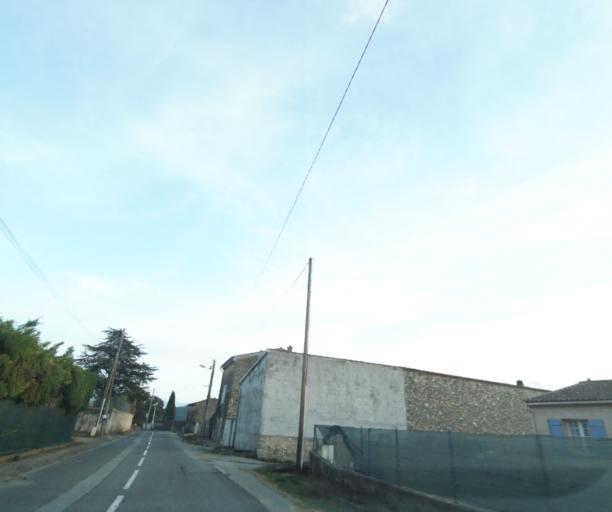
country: FR
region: Provence-Alpes-Cote d'Azur
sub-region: Departement du Var
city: Trans-en-Provence
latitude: 43.5012
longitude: 6.4926
